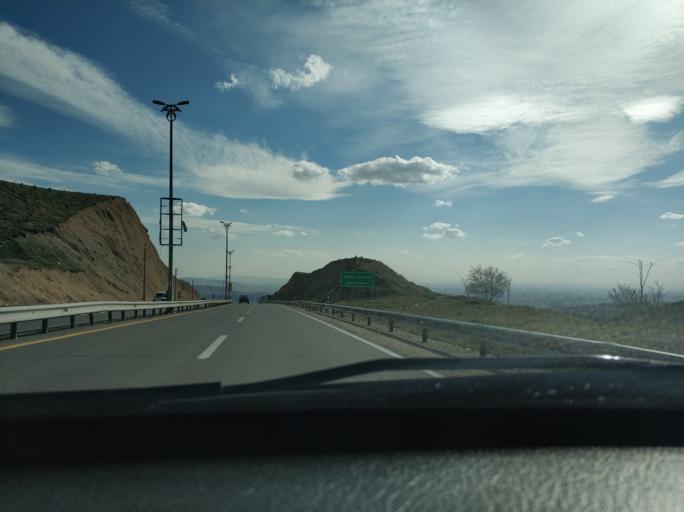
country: IR
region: Tehran
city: Tajrish
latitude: 35.7905
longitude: 51.5682
